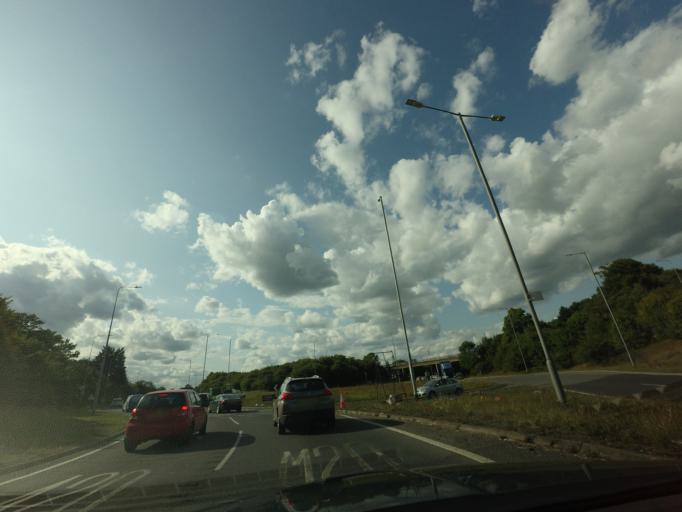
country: GB
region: England
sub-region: Kent
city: Harrietsham
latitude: 51.2607
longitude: 0.6130
